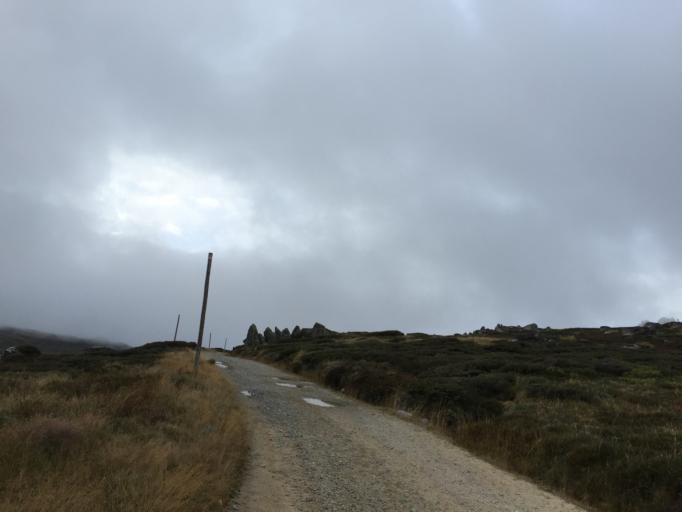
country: AU
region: New South Wales
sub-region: Snowy River
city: Jindabyne
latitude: -36.4565
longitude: 148.3014
